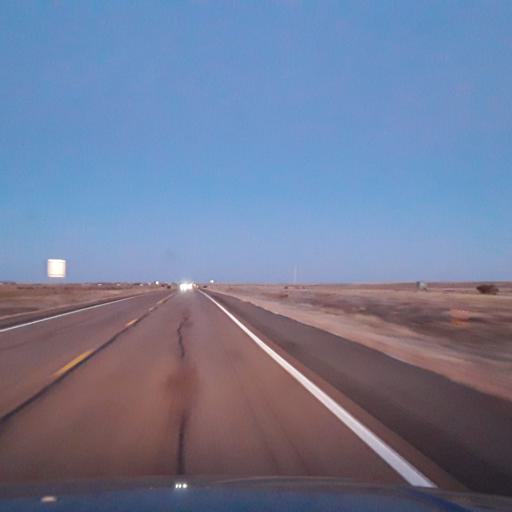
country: US
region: New Mexico
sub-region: Guadalupe County
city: Santa Rosa
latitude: 34.7690
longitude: -104.9698
